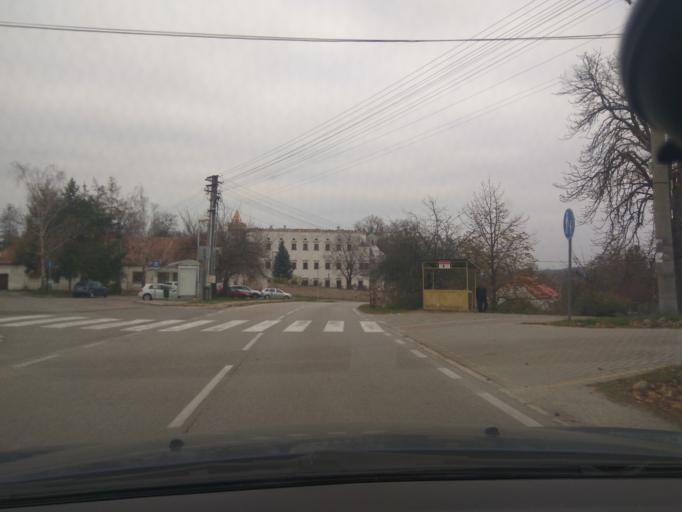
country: SK
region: Trnavsky
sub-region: Okres Trnava
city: Piestany
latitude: 48.6029
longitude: 17.8620
